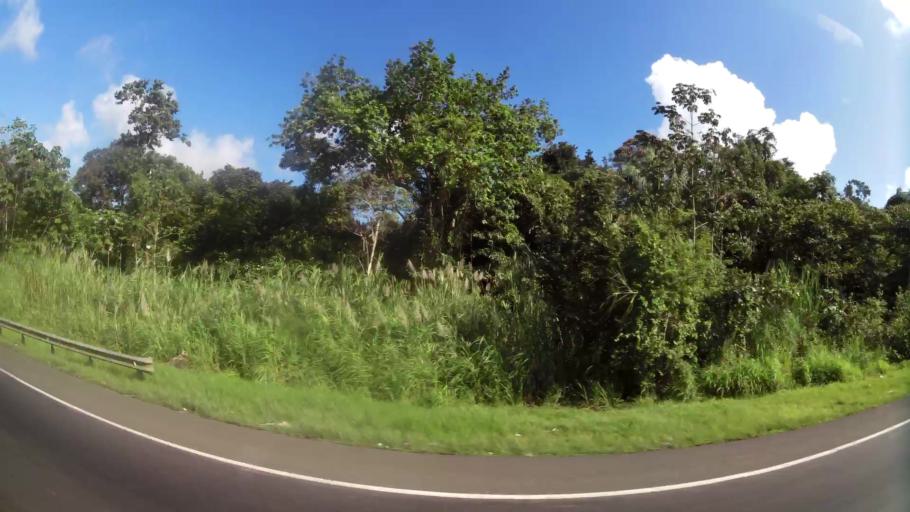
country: PA
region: Panama
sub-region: Distrito Arraijan
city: Arraijan
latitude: 8.9550
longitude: -79.6443
